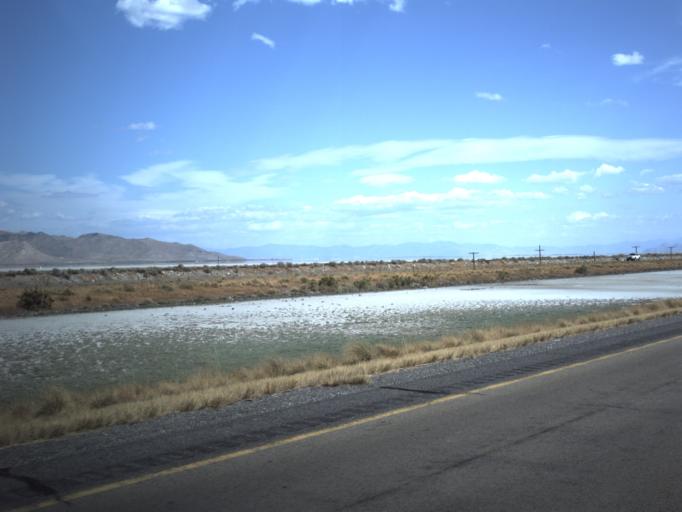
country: US
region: Utah
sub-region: Tooele County
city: Grantsville
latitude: 40.7393
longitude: -112.6214
